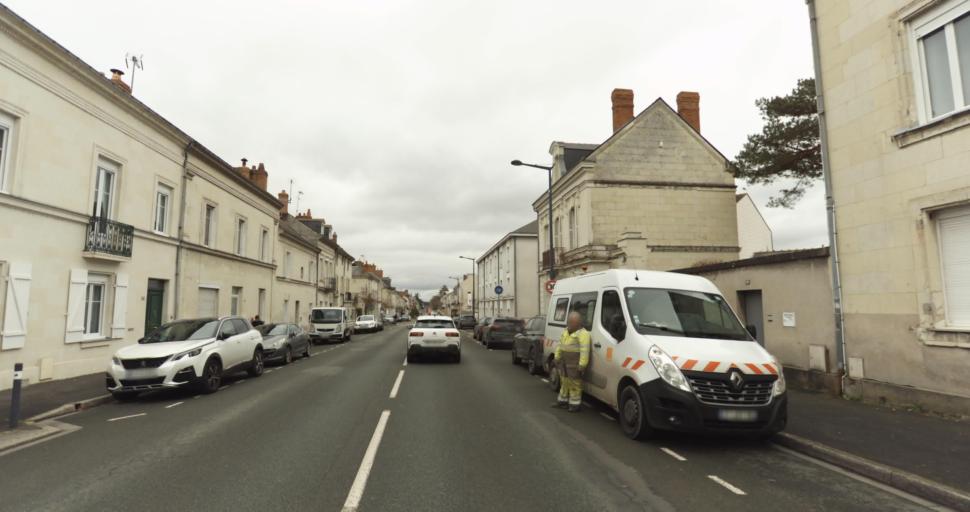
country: FR
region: Pays de la Loire
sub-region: Departement de Maine-et-Loire
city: Saumur
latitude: 47.2483
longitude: -0.0917
